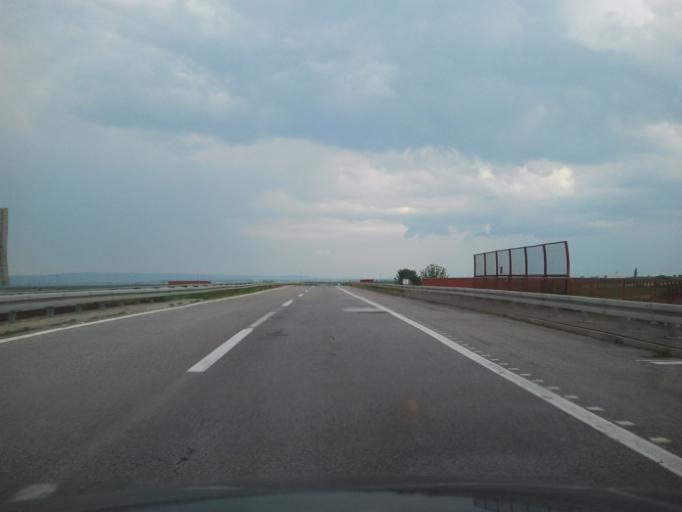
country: RS
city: Ravnje
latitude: 45.0420
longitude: 19.4043
